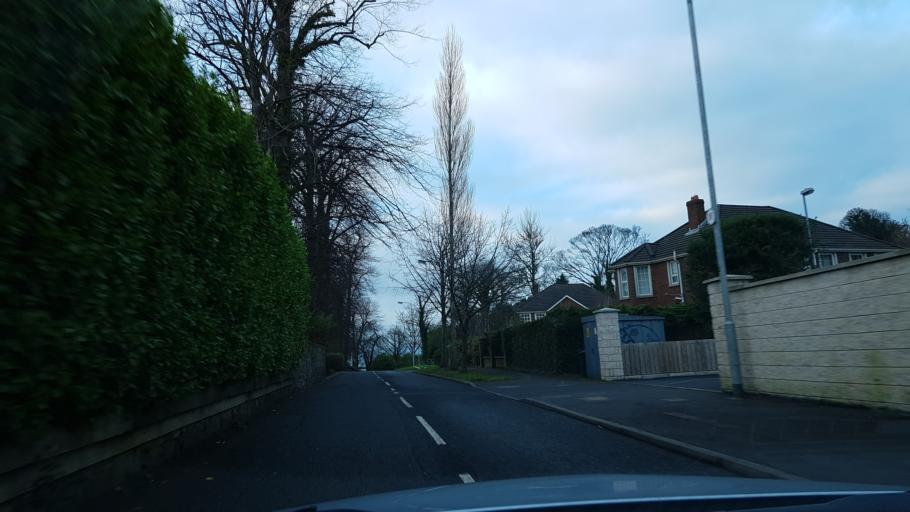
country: GB
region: Northern Ireland
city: Holywood
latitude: 54.6415
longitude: -5.8211
